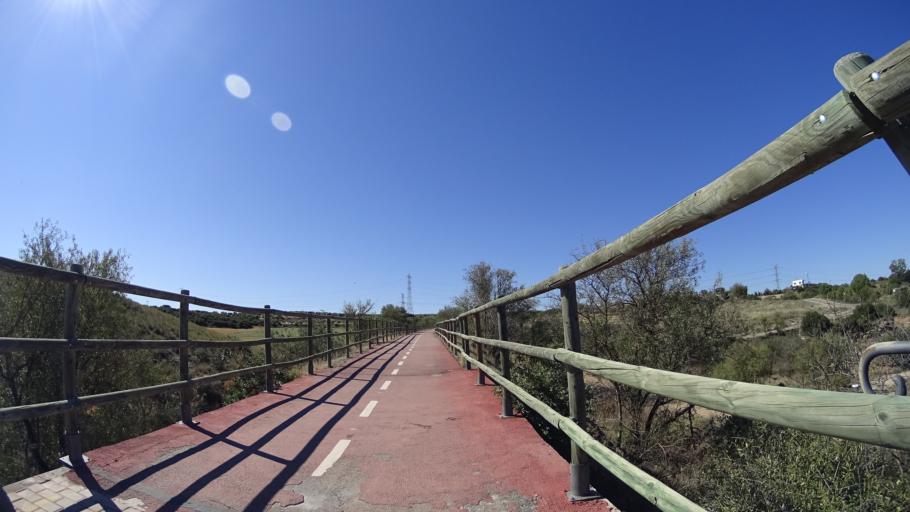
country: ES
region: Madrid
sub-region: Provincia de Madrid
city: Morata de Tajuna
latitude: 40.2614
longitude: -3.4687
